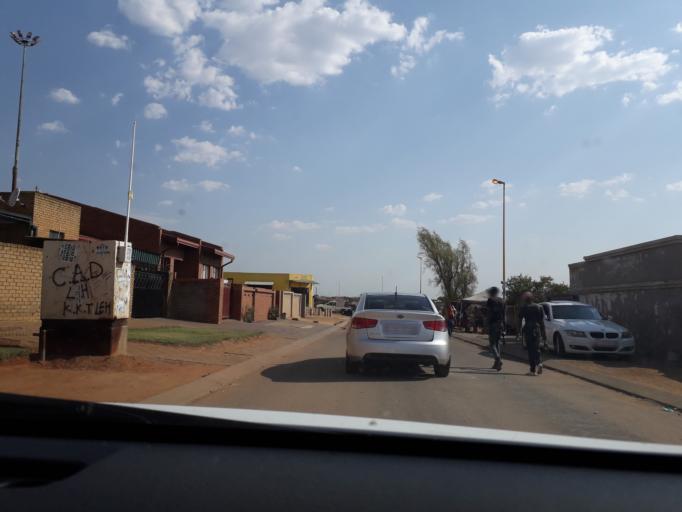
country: ZA
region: Gauteng
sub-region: Ekurhuleni Metropolitan Municipality
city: Tembisa
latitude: -26.0154
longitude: 28.2248
